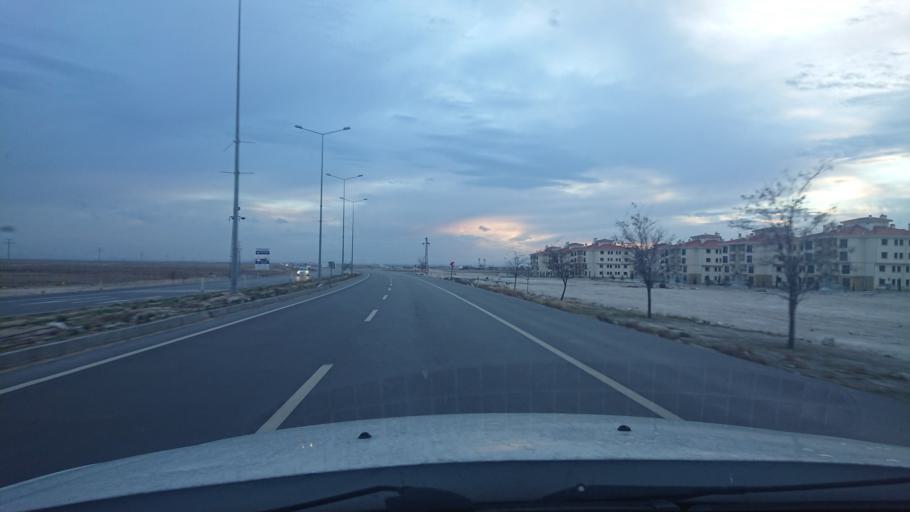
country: TR
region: Aksaray
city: Sultanhani
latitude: 38.2515
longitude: 33.5686
